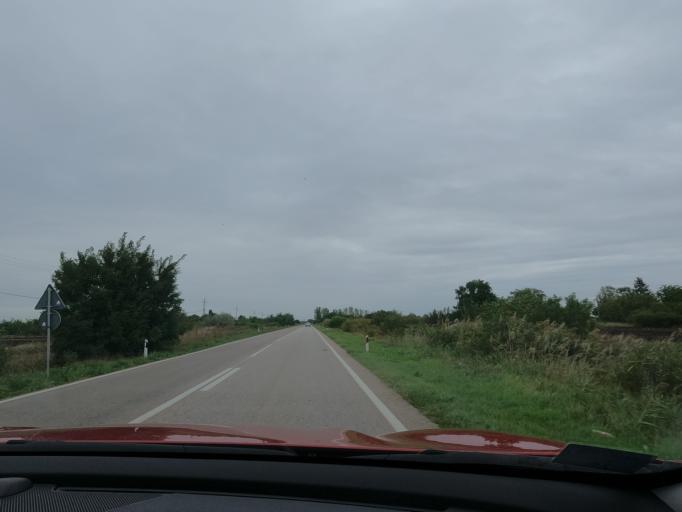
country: RS
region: Autonomna Pokrajina Vojvodina
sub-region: Severnobanatski Okrug
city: Kikinda
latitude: 45.7697
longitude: 20.4243
